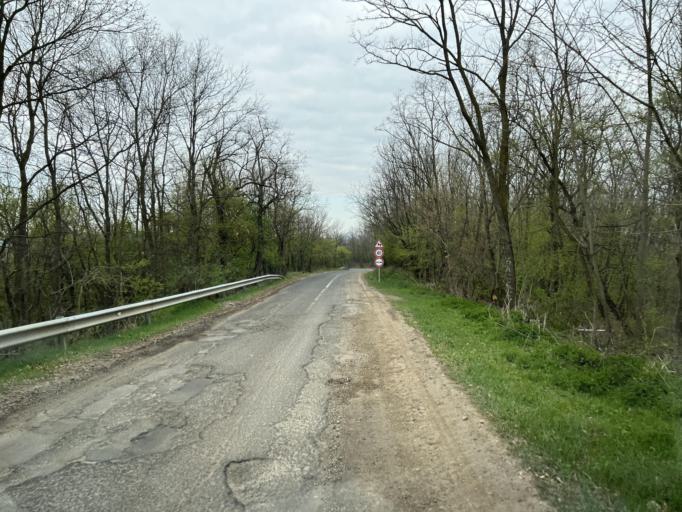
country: HU
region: Pest
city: Acsa
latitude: 47.7899
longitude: 19.4056
